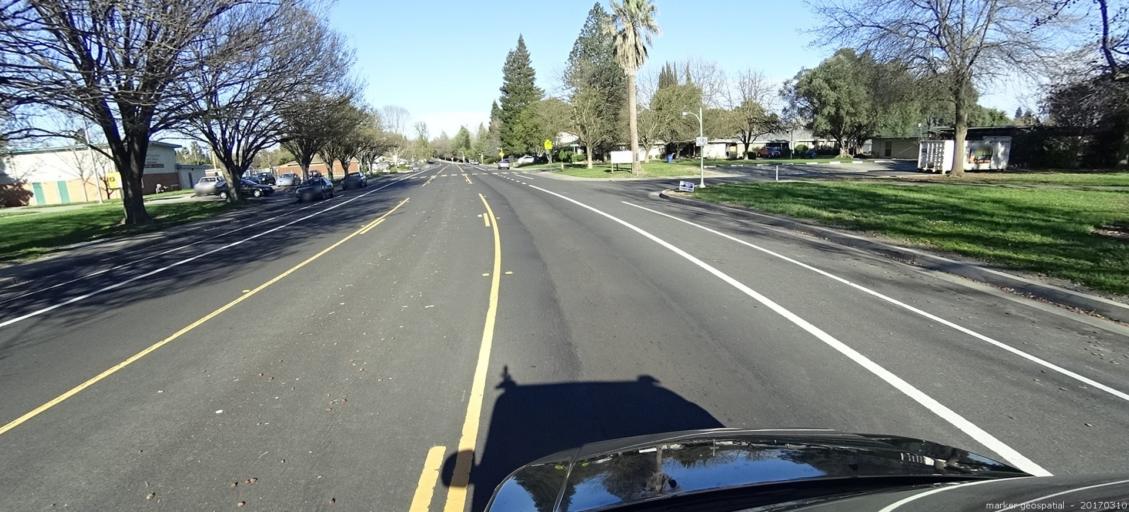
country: US
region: California
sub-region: Sacramento County
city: Parkway
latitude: 38.5067
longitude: -121.5271
